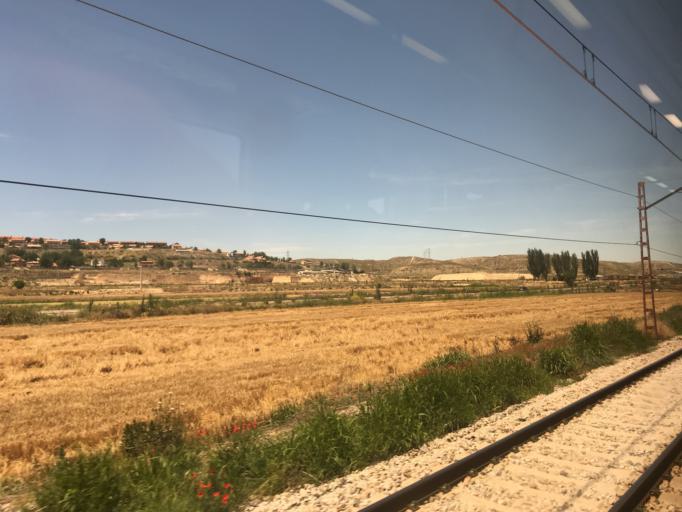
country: ES
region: Madrid
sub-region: Provincia de Madrid
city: Ciempozuelos
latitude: 40.1059
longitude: -3.6247
